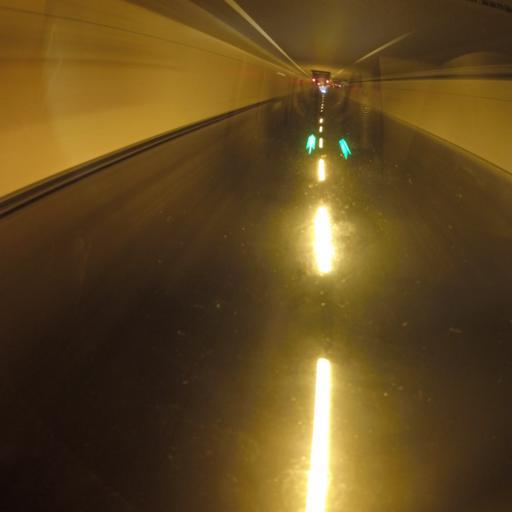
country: PT
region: Madeira
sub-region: Funchal
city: Nossa Senhora do Monte
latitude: 32.6631
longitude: -16.9159
